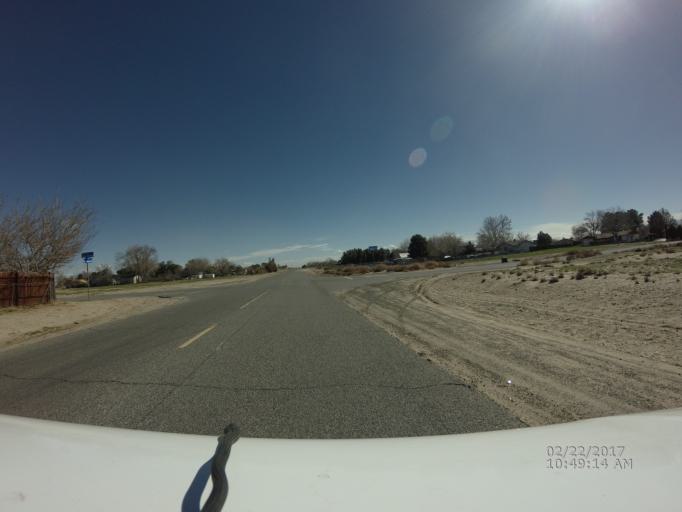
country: US
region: California
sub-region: Los Angeles County
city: Lake Los Angeles
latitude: 34.6238
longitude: -117.8228
